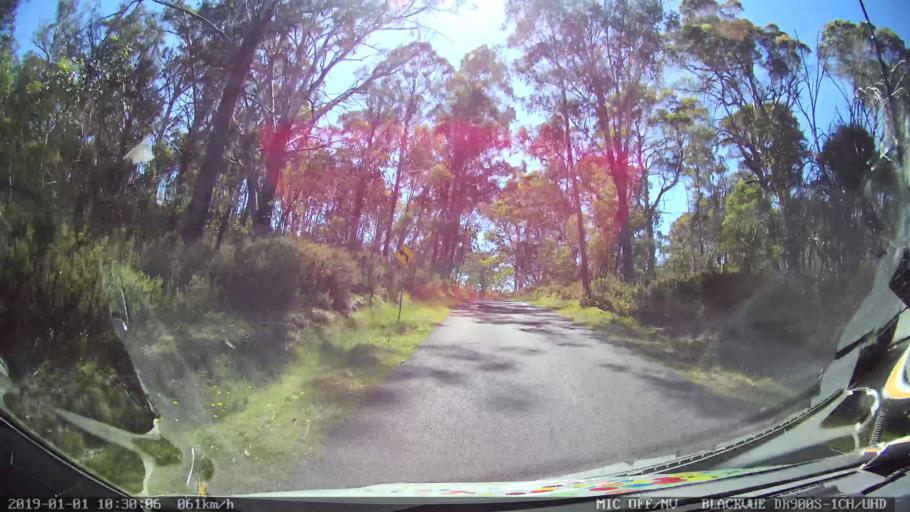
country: AU
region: New South Wales
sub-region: Snowy River
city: Jindabyne
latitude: -36.0527
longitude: 148.2549
